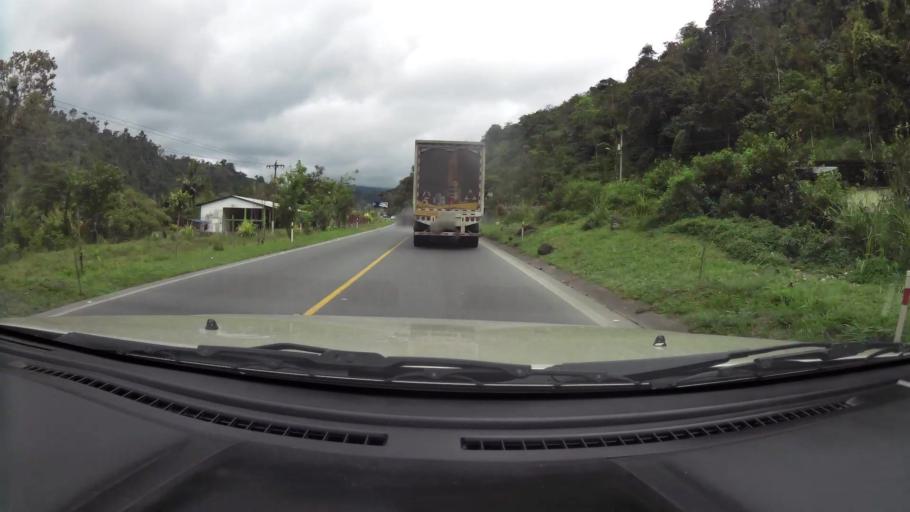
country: EC
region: Santo Domingo de los Tsachilas
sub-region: Canton Santo Domingo de los Colorados
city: Santo Domingo de los Colorados
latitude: -0.3014
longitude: -79.0478
